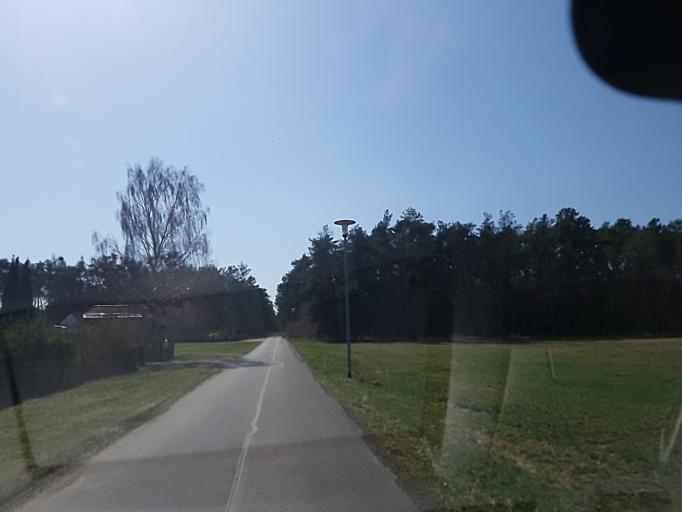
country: DE
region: Brandenburg
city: Schonborn
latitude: 51.5912
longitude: 13.4905
